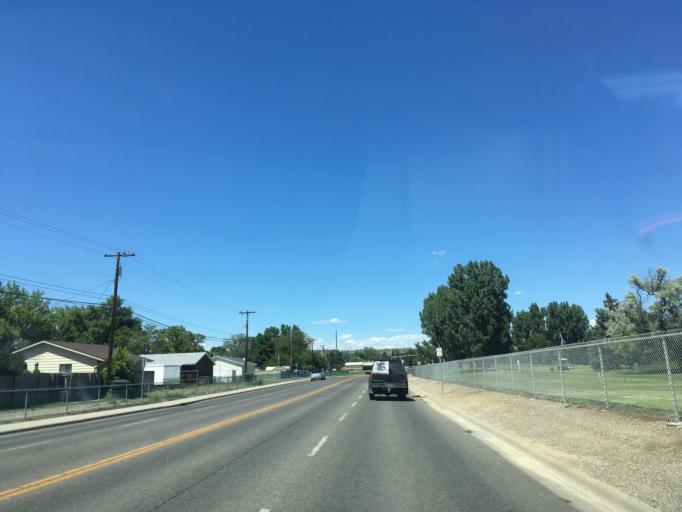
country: US
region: Montana
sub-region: Yellowstone County
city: Billings
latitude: 45.7672
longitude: -108.5650
